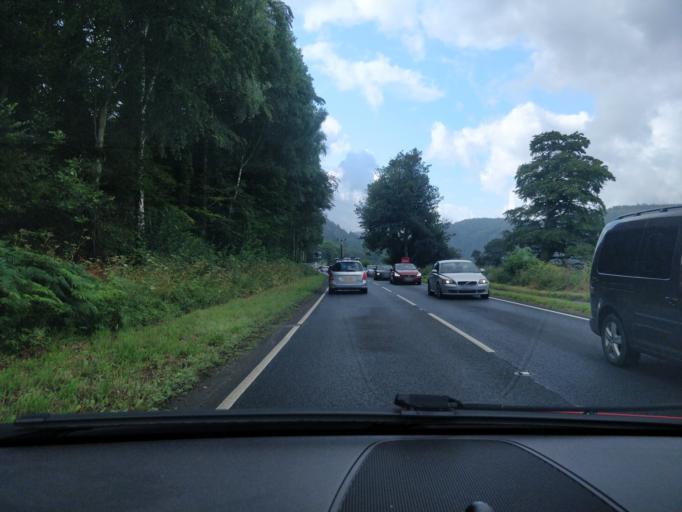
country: GB
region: Wales
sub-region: Conwy
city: Betws-y-Coed
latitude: 53.1041
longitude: -3.7867
